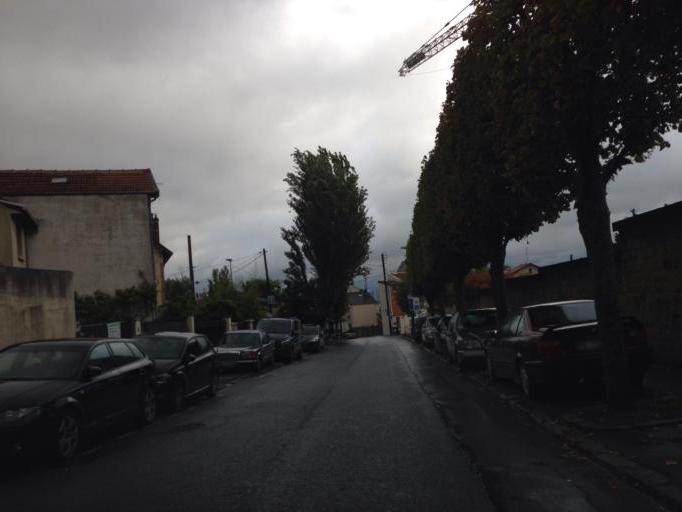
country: FR
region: Ile-de-France
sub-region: Departement des Hauts-de-Seine
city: Clamart
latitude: 48.8147
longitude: 2.2535
